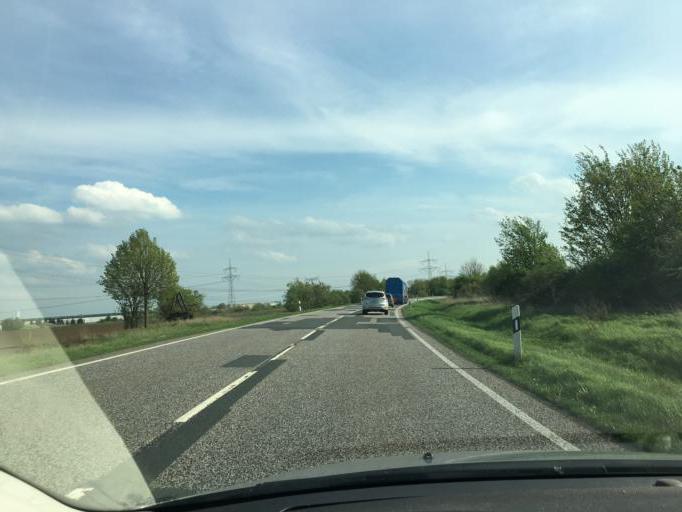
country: DE
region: Saxony-Anhalt
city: Meitzendorf
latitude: 52.2133
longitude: 11.5461
